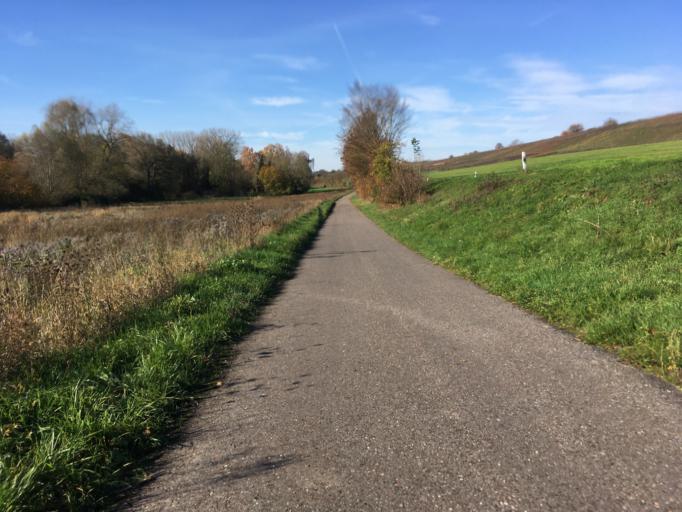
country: DE
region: Baden-Wuerttemberg
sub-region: Karlsruhe Region
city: Sulzfeld
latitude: 49.1118
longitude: 8.8476
